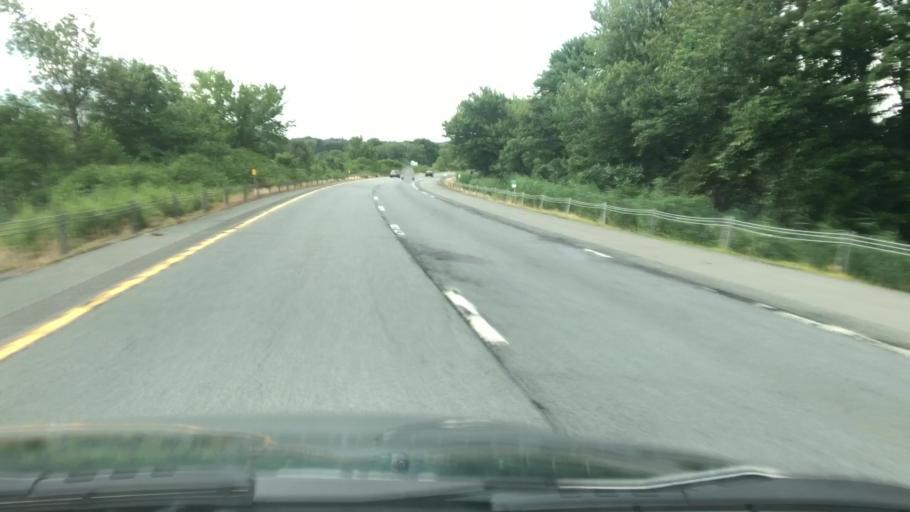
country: US
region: New York
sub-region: Orange County
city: Port Jervis
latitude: 41.3802
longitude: -74.5994
